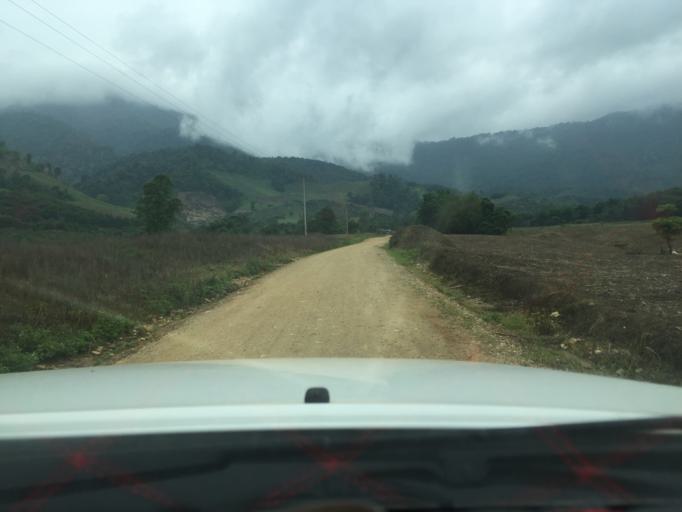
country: TH
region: Phayao
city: Phu Sang
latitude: 19.7427
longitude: 100.4367
